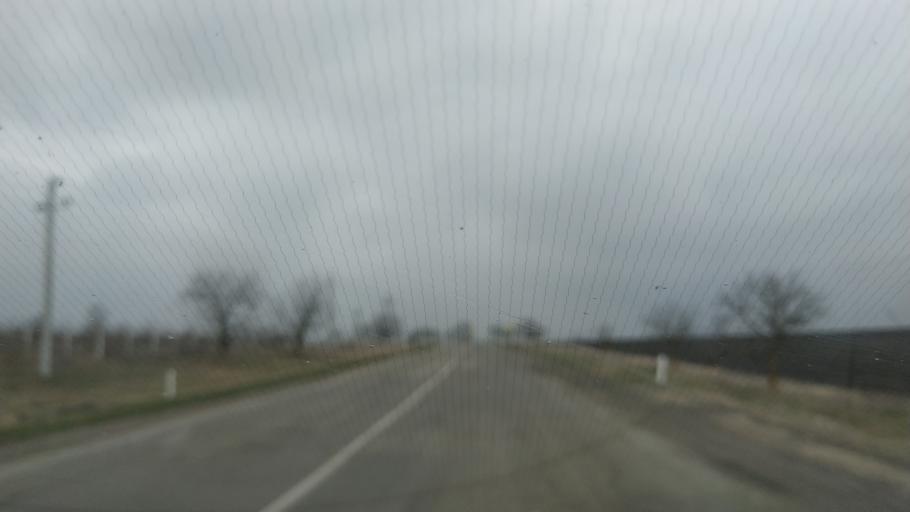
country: MD
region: Gagauzia
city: Comrat
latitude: 46.2685
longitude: 28.7328
